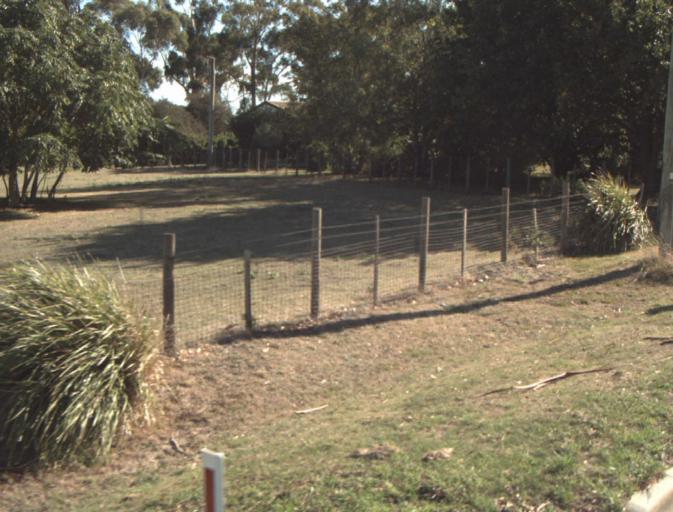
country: AU
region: Tasmania
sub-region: Launceston
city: Mayfield
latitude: -41.3429
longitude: 147.0913
